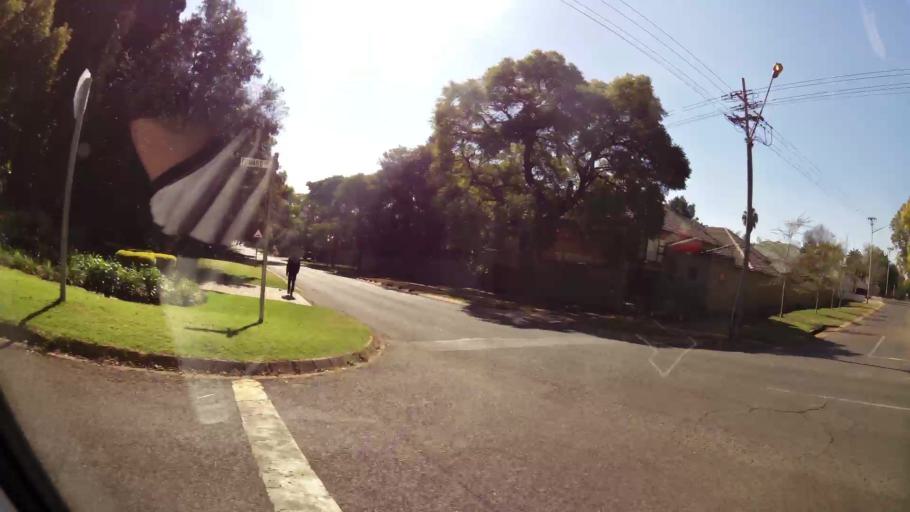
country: ZA
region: Gauteng
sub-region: City of Tshwane Metropolitan Municipality
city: Pretoria
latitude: -25.7822
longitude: 28.2424
